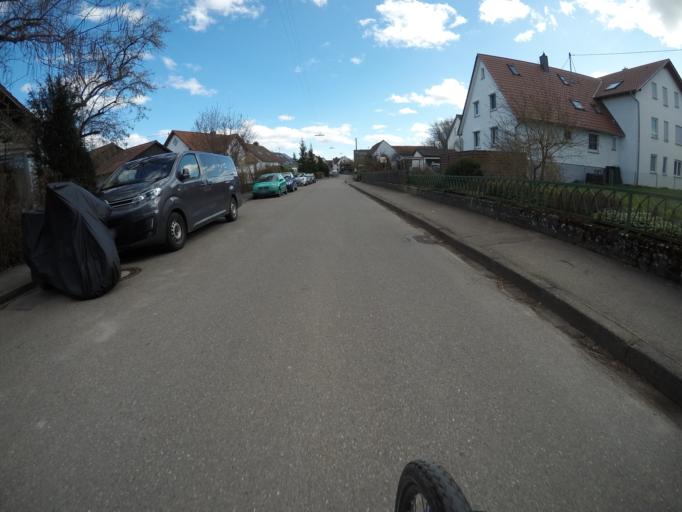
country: DE
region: Baden-Wuerttemberg
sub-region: Regierungsbezirk Stuttgart
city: Leinfelden-Echterdingen
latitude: 48.6717
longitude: 9.1615
